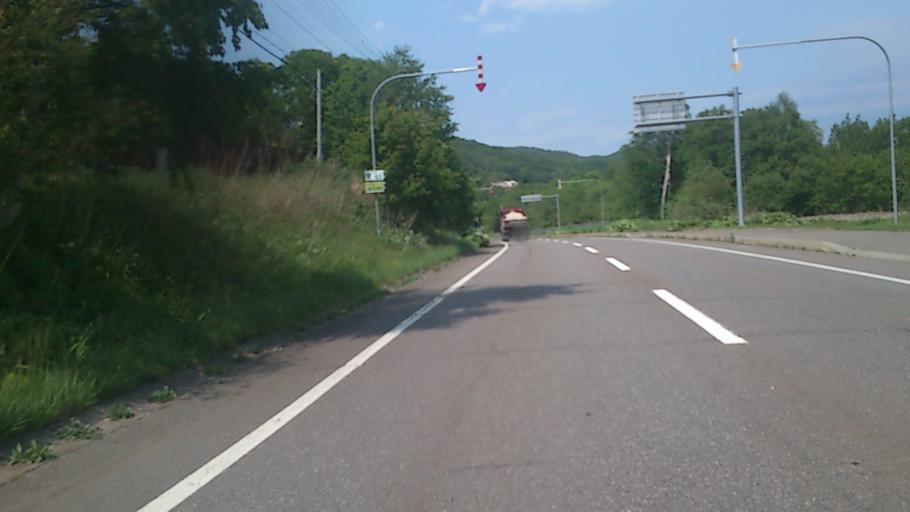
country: JP
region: Hokkaido
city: Otofuke
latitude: 43.2506
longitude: 143.5644
